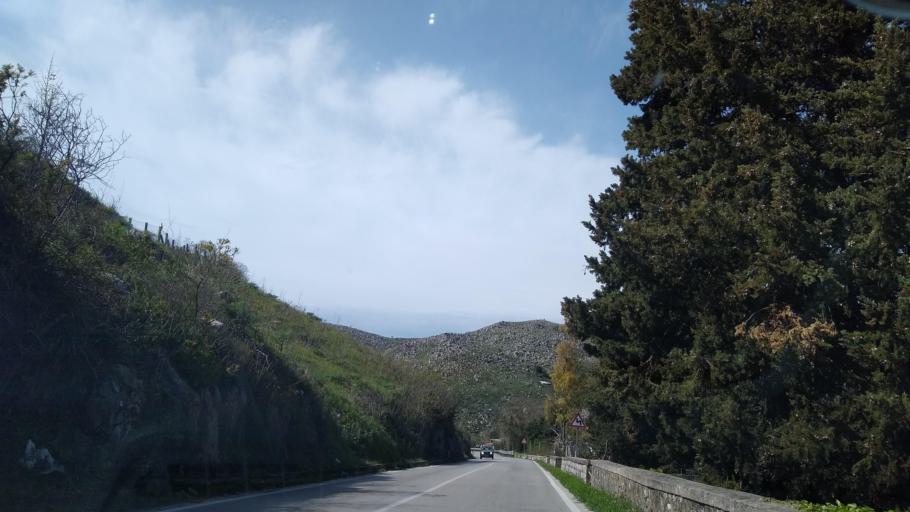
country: IT
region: Sicily
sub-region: Palermo
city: Pioppo
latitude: 38.0442
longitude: 13.1991
